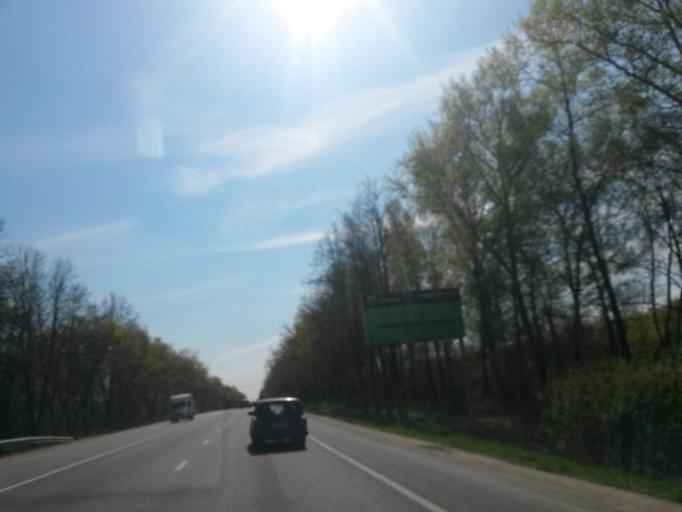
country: RU
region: Moskovskaya
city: L'vovskiy
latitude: 55.3022
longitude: 37.5284
